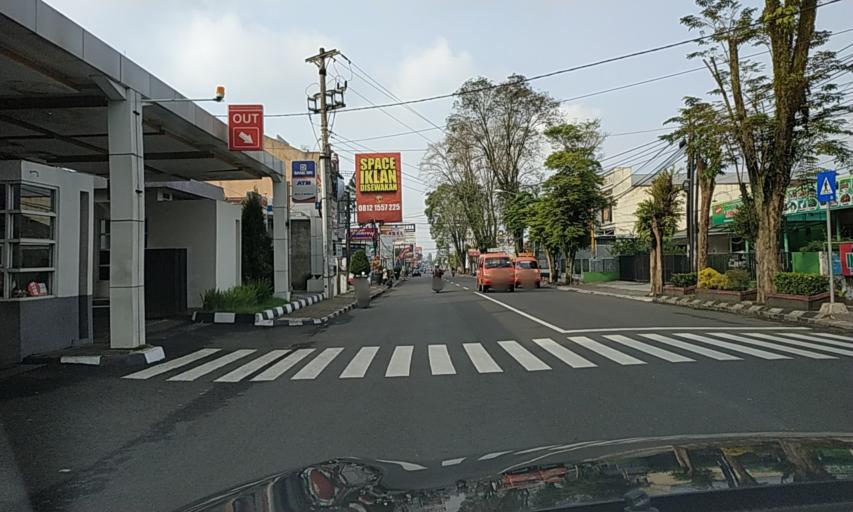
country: ID
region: Central Java
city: Purwokerto
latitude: -7.4180
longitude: 109.2446
